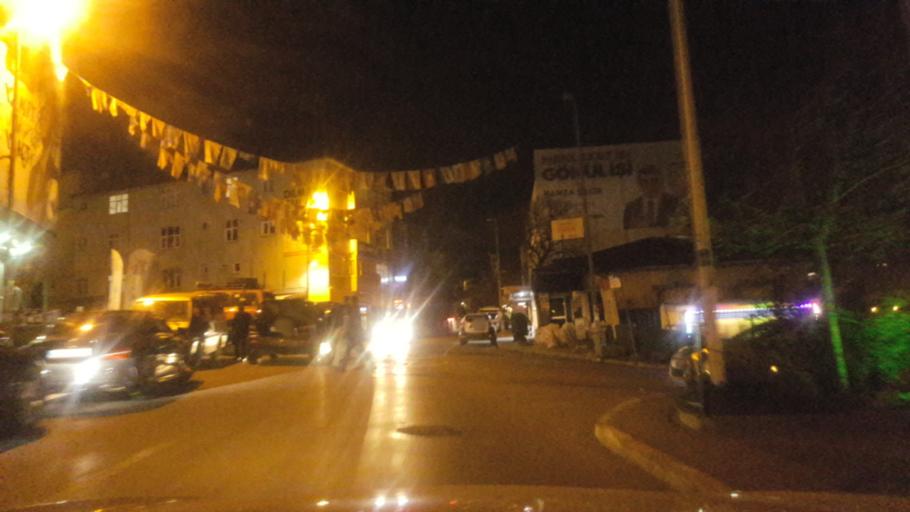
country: TR
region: Kocaeli
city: Tavsanli
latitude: 40.7880
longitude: 29.5333
